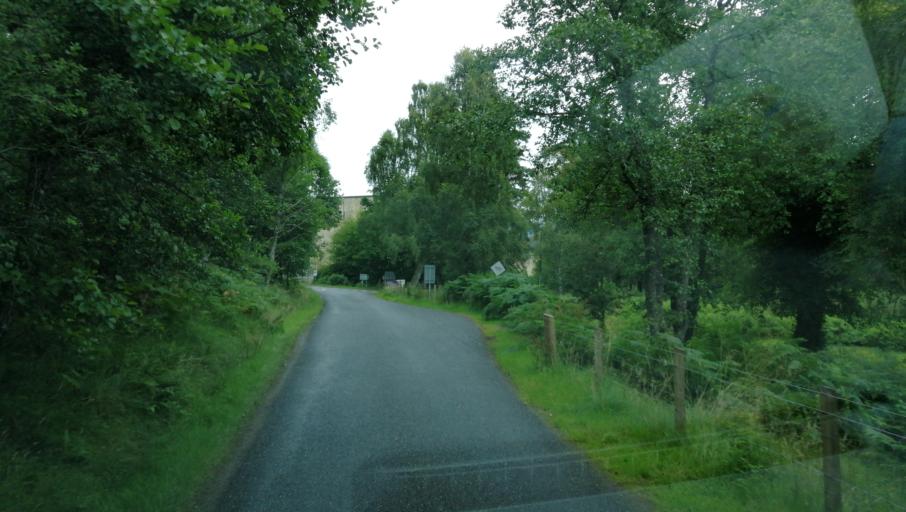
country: GB
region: Scotland
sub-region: Highland
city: Beauly
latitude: 57.3247
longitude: -4.7957
